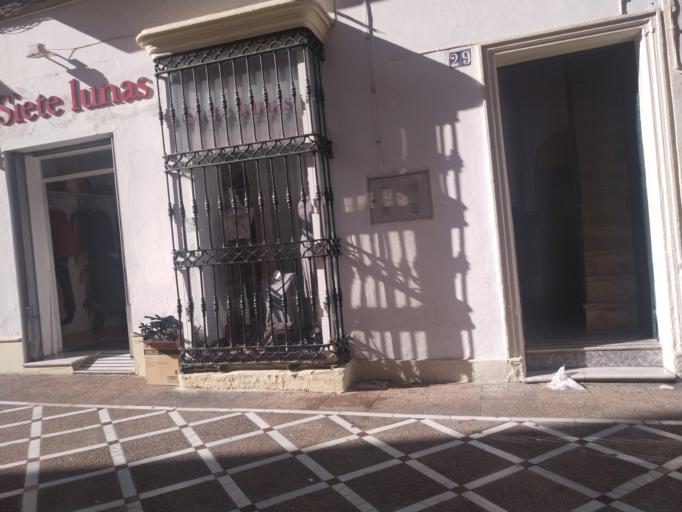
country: ES
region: Andalusia
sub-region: Provincia de Cadiz
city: San Fernando
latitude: 36.4708
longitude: -6.1954
